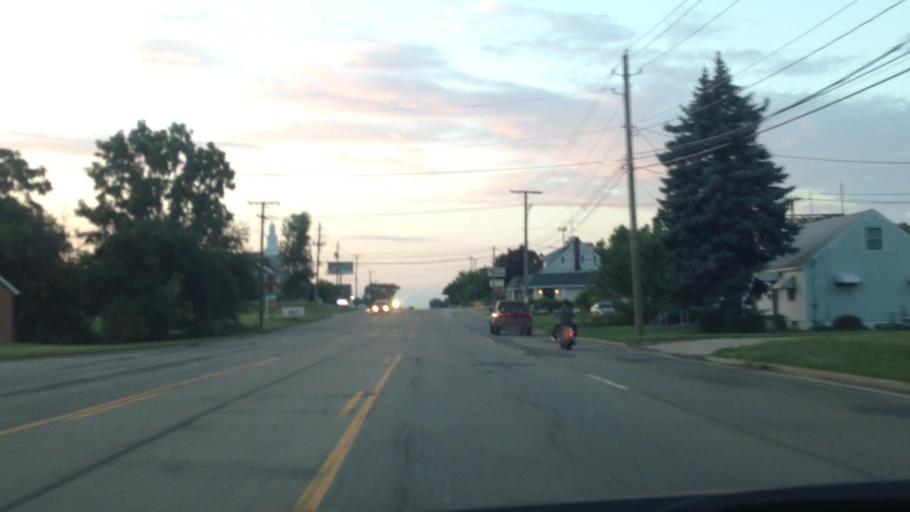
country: US
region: Ohio
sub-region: Stark County
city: Genoa
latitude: 40.8071
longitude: -81.4257
